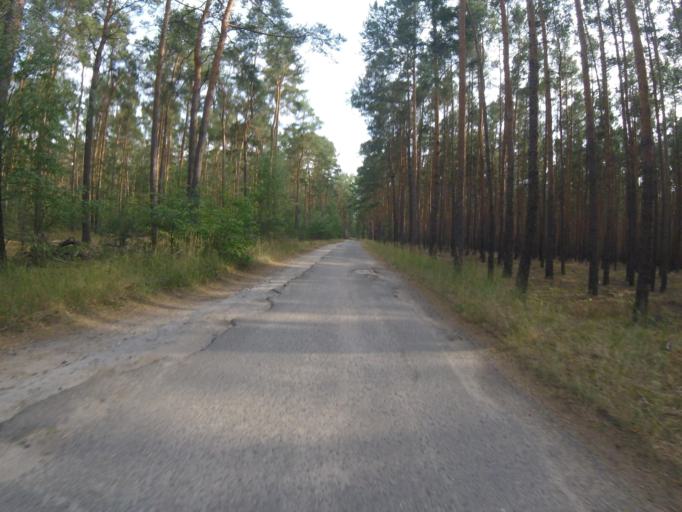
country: DE
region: Brandenburg
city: Gross Koris
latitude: 52.2147
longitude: 13.7385
